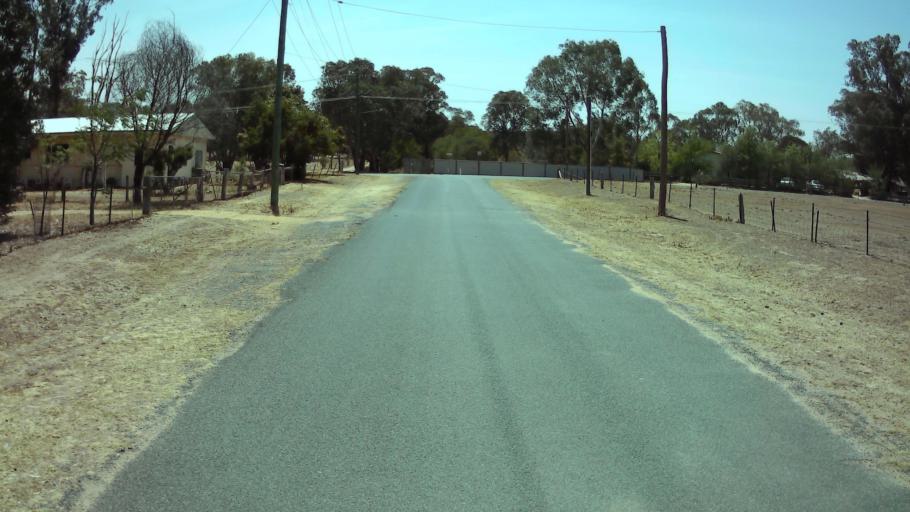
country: AU
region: New South Wales
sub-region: Weddin
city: Grenfell
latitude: -33.8892
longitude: 148.1693
